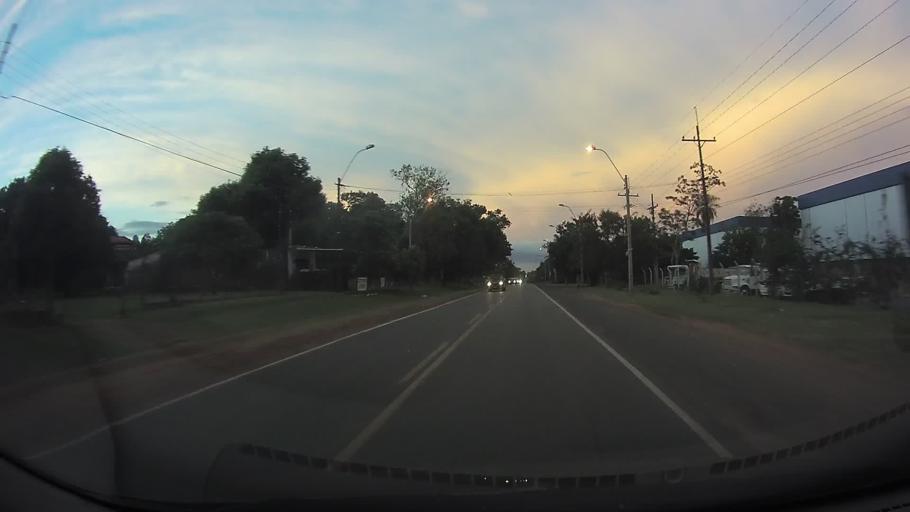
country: PY
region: Central
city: Ita
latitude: -25.4915
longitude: -57.3593
